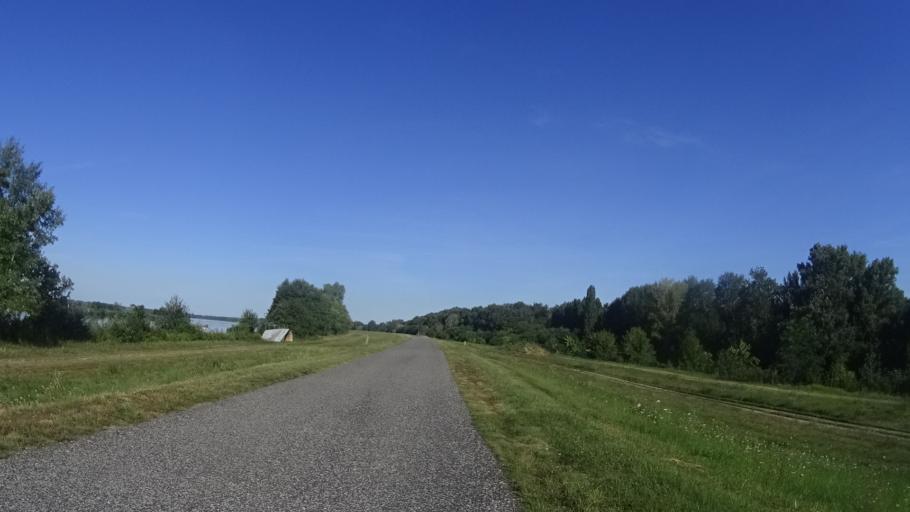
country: SK
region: Bratislavsky
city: Dunajska Luzna
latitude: 48.0560
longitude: 17.2291
